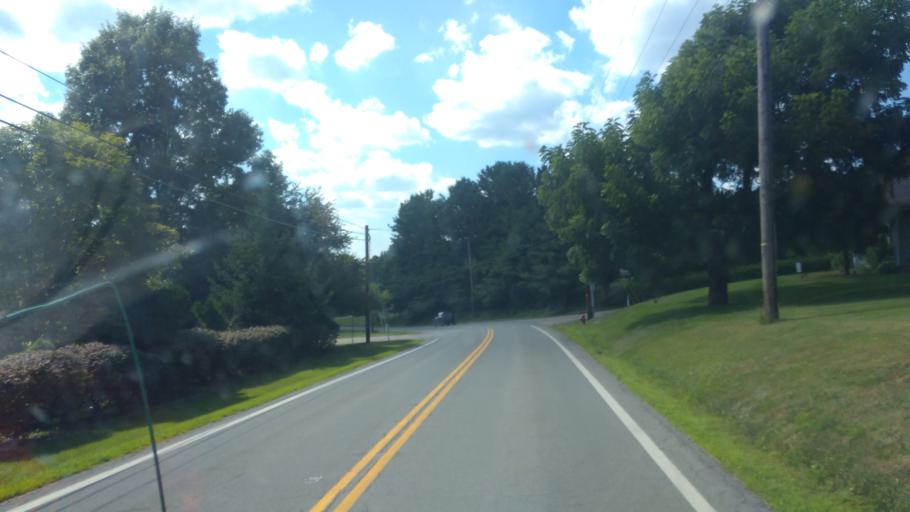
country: US
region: Ohio
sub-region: Tuscarawas County
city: Strasburg
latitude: 40.6205
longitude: -81.4268
